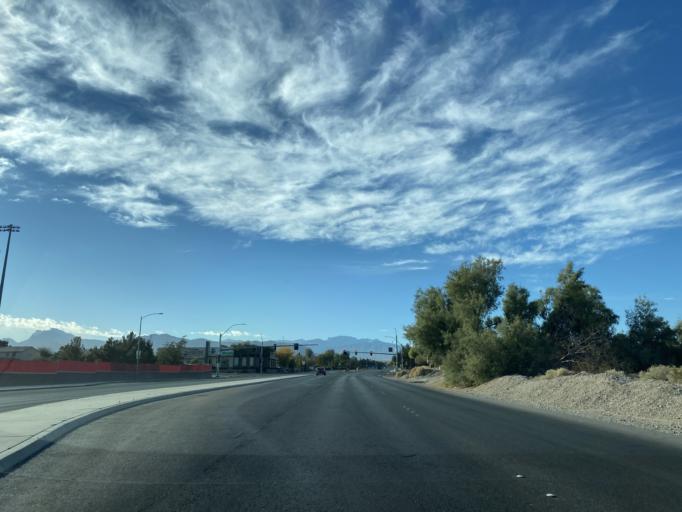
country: US
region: Nevada
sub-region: Clark County
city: North Las Vegas
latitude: 36.3052
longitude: -115.2585
